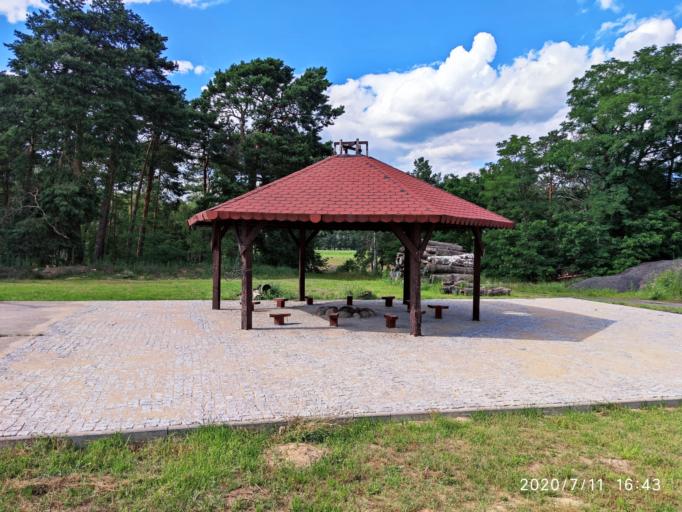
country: PL
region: Lubusz
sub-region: Powiat krosnienski
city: Maszewo
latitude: 52.0415
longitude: 14.9914
